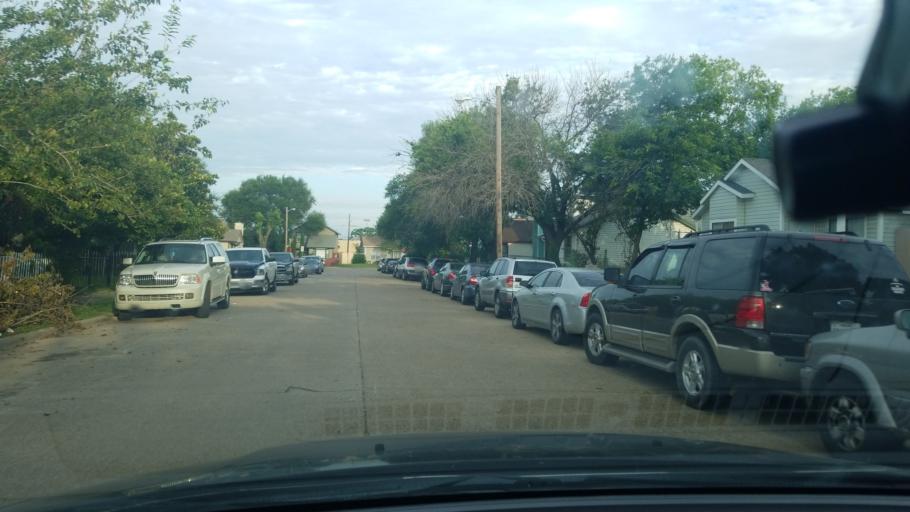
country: US
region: Texas
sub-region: Dallas County
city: Balch Springs
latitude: 32.7468
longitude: -96.6454
